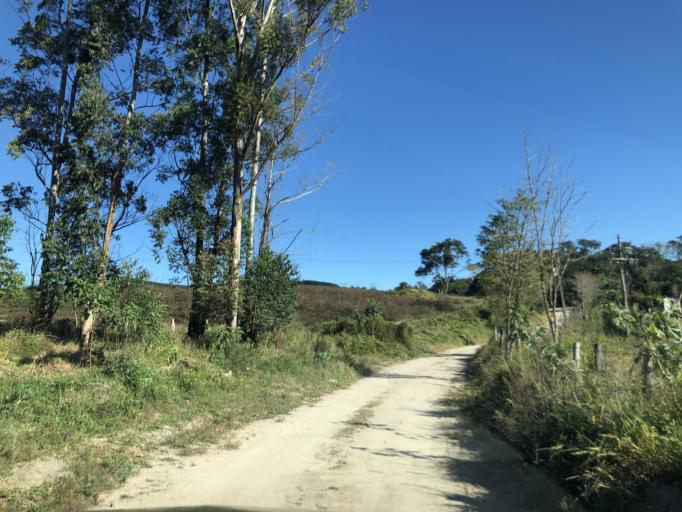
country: BR
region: Sao Paulo
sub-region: Pilar Do Sul
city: Pilar do Sul
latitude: -23.8246
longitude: -47.6277
